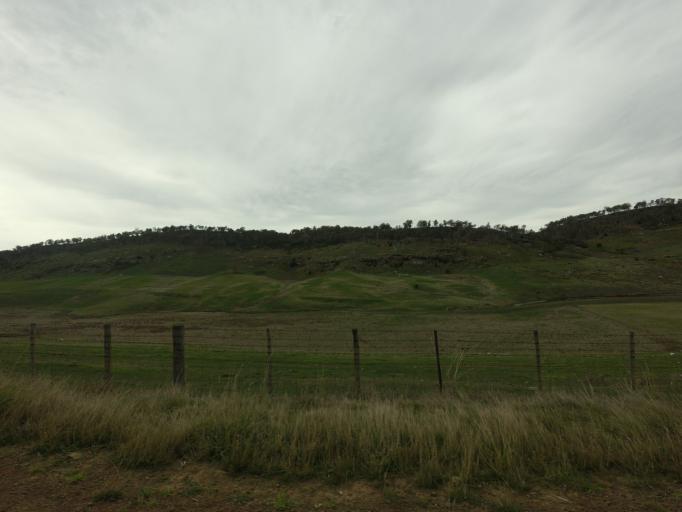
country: AU
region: Tasmania
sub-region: Derwent Valley
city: New Norfolk
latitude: -42.4020
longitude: 146.9202
